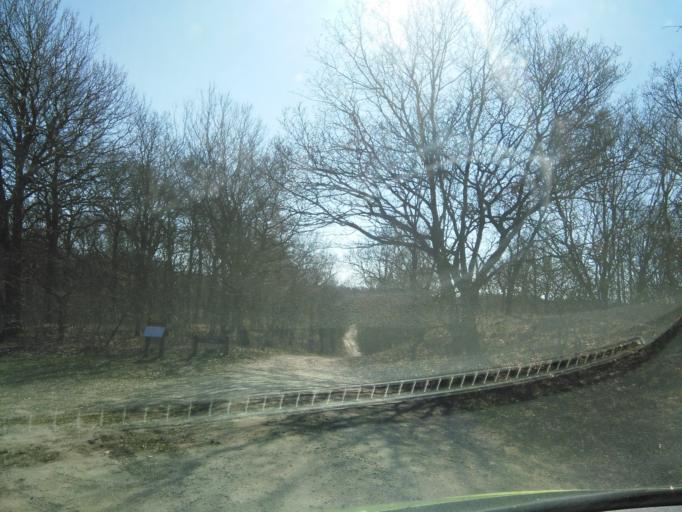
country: DK
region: Central Jutland
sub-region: Hedensted Kommune
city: Torring
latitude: 55.9121
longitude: 9.4010
